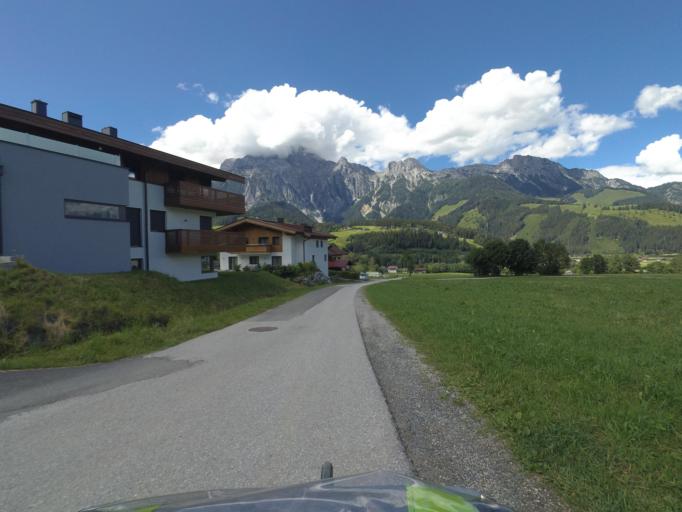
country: AT
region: Salzburg
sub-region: Politischer Bezirk Zell am See
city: Leogang
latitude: 47.4332
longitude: 12.7637
